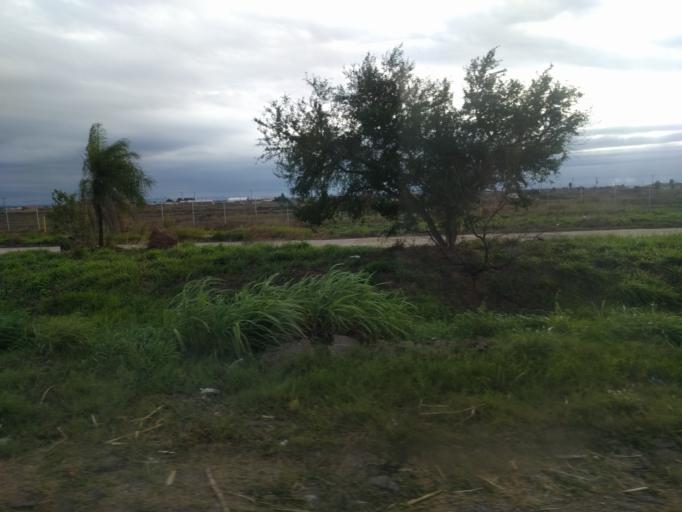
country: BO
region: Santa Cruz
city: La Belgica
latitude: -17.6015
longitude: -63.1592
